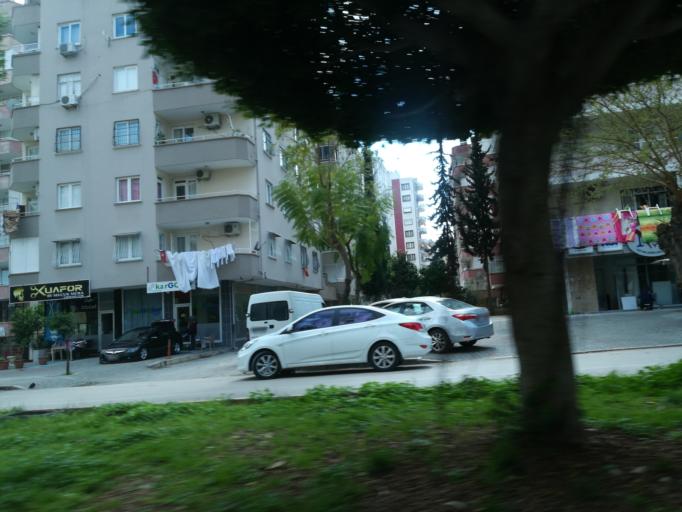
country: TR
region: Adana
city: Adana
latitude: 37.0310
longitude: 35.3021
